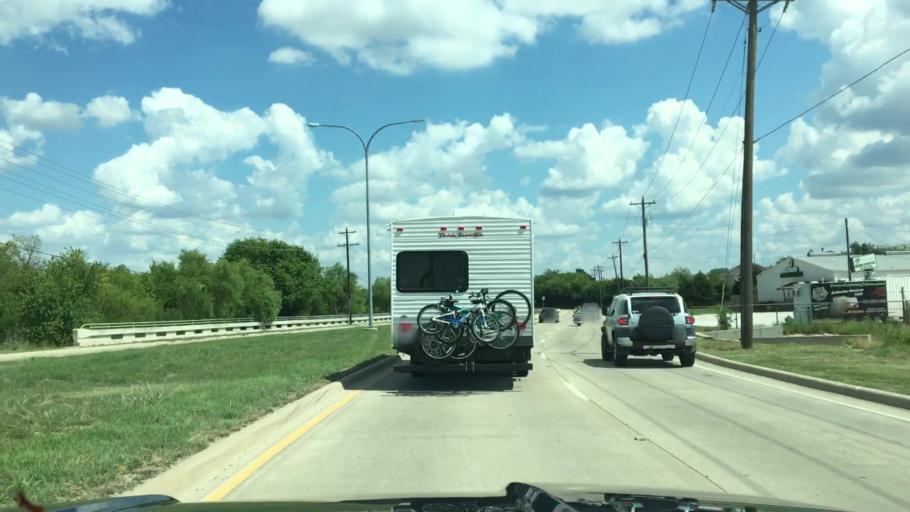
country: US
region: Texas
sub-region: Tarrant County
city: Keller
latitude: 32.9323
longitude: -97.3001
